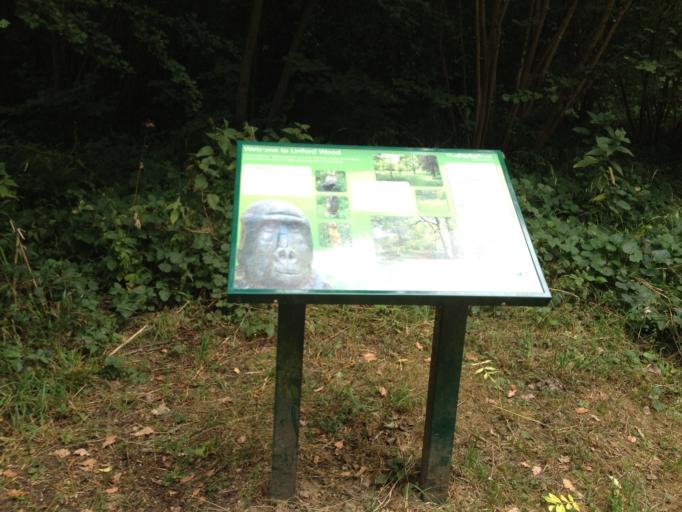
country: GB
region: England
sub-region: Milton Keynes
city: Milton Keynes
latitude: 52.0547
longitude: -0.7679
